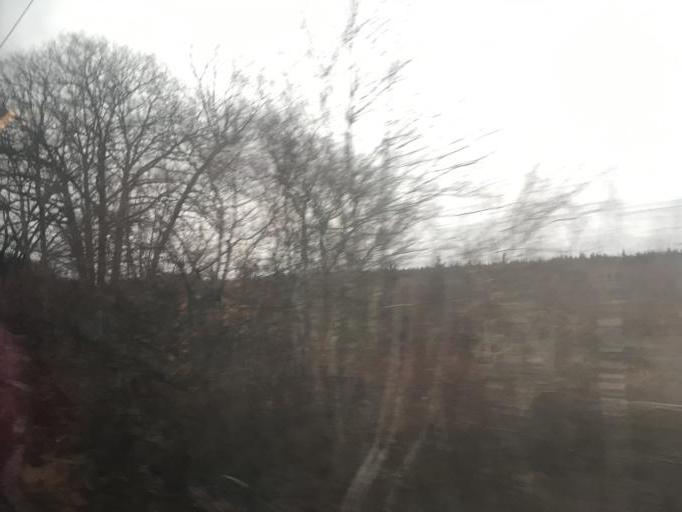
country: US
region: Massachusetts
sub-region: Bristol County
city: Attleboro
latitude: 41.9580
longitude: -71.2729
